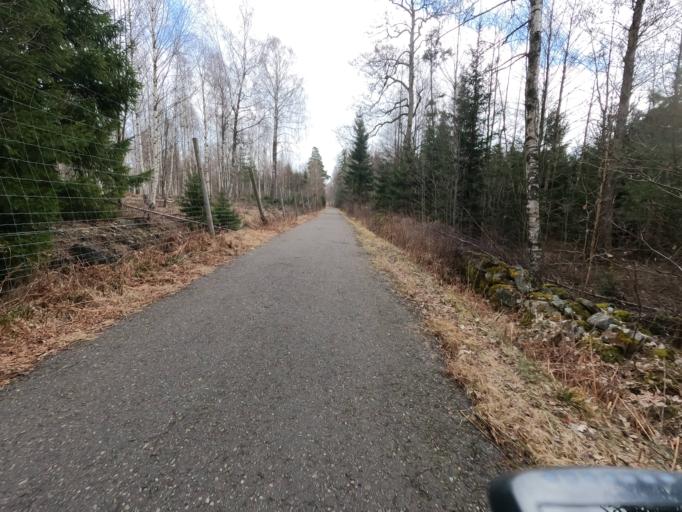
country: SE
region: Joenkoeping
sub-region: Varnamo Kommun
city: Rydaholm
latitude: 56.8556
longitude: 14.1848
